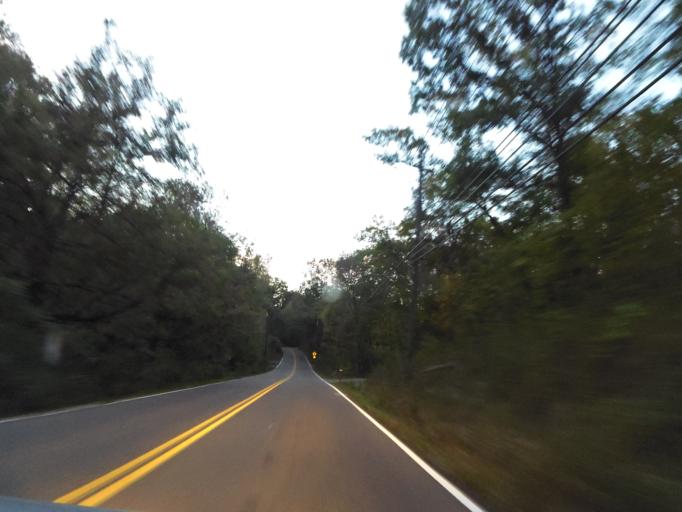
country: US
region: Tennessee
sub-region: Knox County
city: Mascot
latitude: 36.0053
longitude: -83.6377
